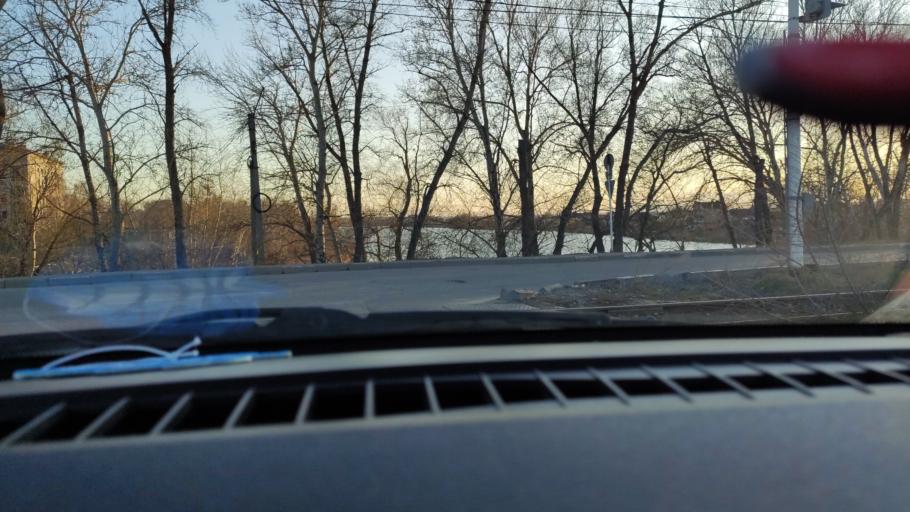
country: RU
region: Saratov
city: Engel's
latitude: 51.5034
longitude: 46.0755
